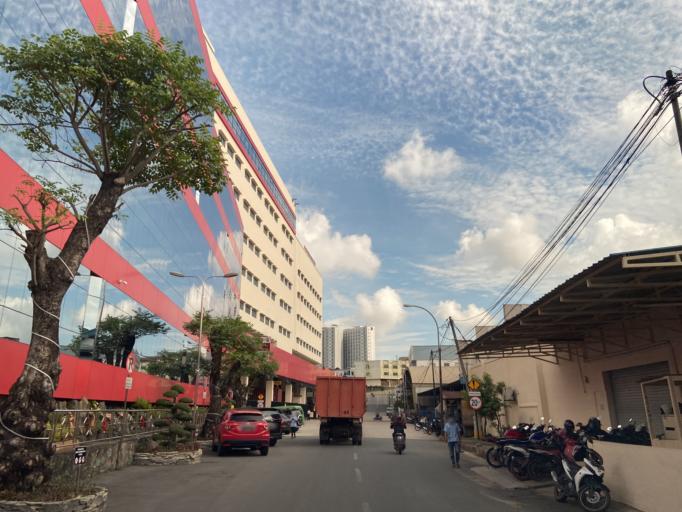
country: SG
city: Singapore
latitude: 1.1403
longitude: 104.0185
